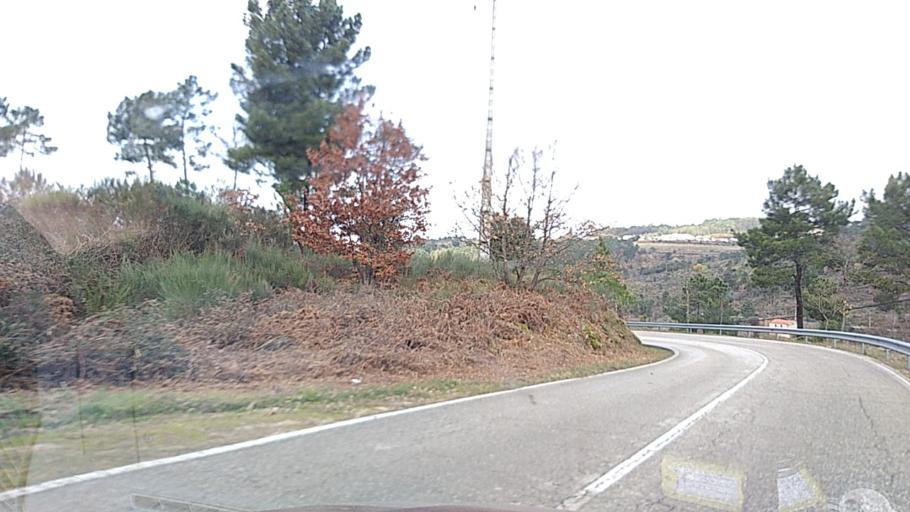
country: PT
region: Viseu
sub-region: Satao
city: Satao
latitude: 40.6638
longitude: -7.6761
